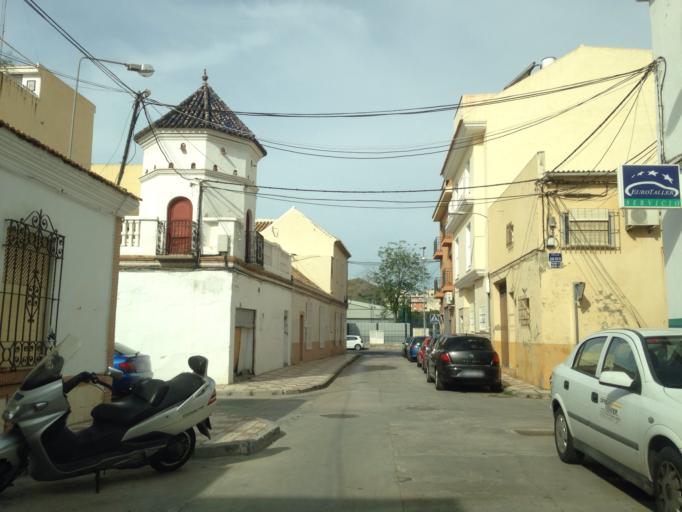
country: ES
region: Andalusia
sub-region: Provincia de Malaga
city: Malaga
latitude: 36.7518
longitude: -4.4227
